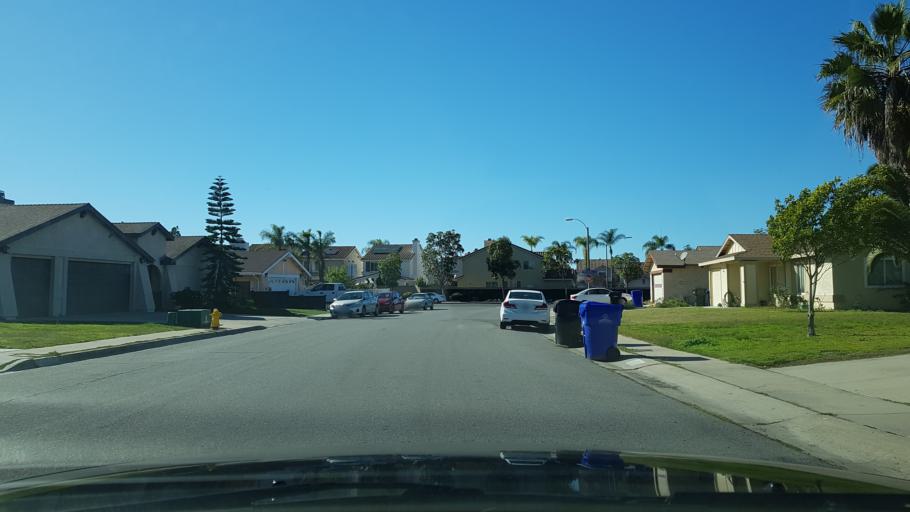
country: US
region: California
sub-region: San Diego County
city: Fairbanks Ranch
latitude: 32.9139
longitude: -117.1348
